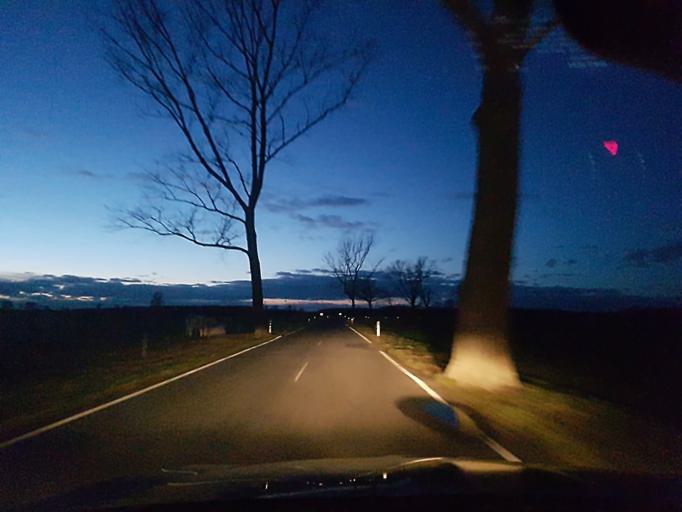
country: DE
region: Brandenburg
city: Schilda
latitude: 51.5550
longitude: 13.3563
